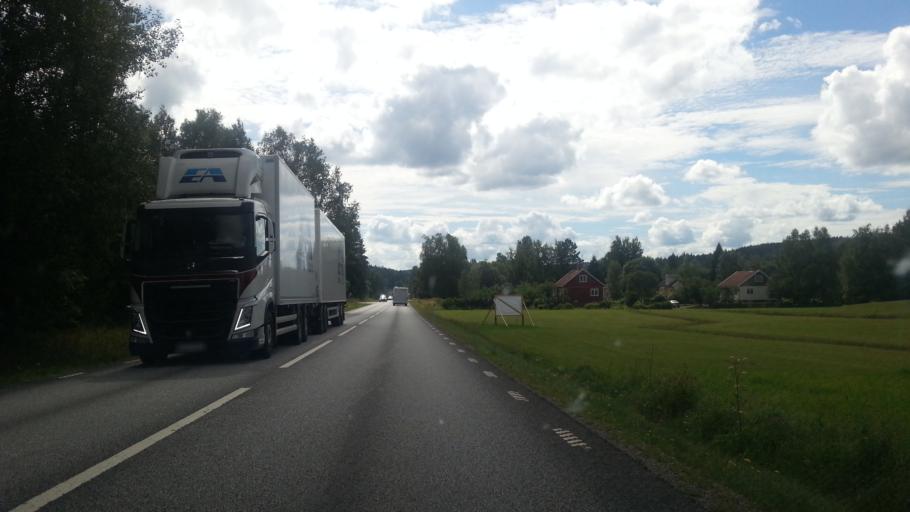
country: SE
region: OErebro
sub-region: Lindesbergs Kommun
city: Stora
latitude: 59.6855
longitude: 15.0972
